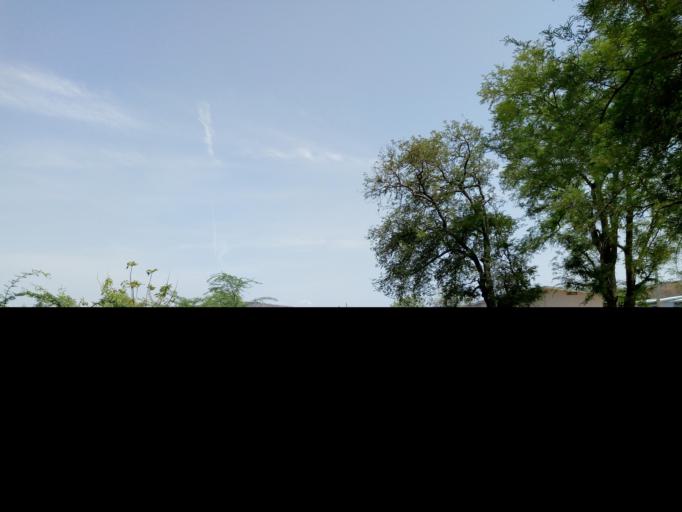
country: IN
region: Andhra Pradesh
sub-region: Prakasam
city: Cumbum
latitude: 15.7088
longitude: 79.0852
